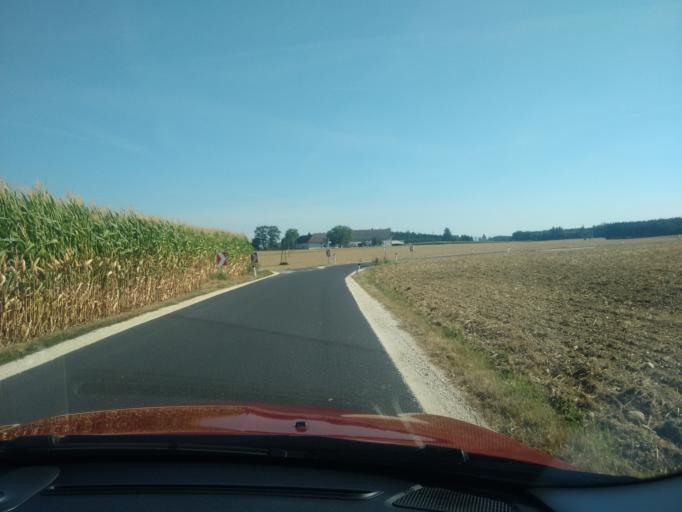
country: AT
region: Upper Austria
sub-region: Wels-Land
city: Sattledt
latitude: 48.0877
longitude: 14.0759
